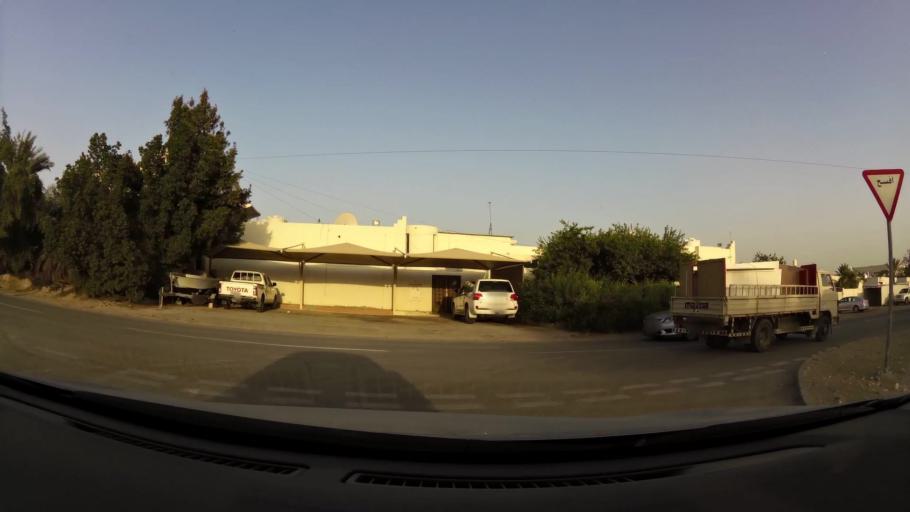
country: QA
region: Baladiyat ar Rayyan
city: Ar Rayyan
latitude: 25.3177
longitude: 51.4581
